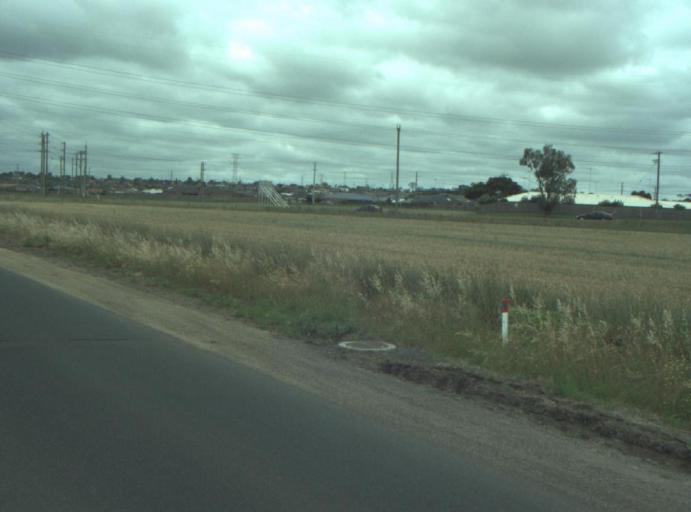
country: AU
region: Victoria
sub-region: Greater Geelong
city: Bell Post Hill
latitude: -38.0796
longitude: 144.3376
